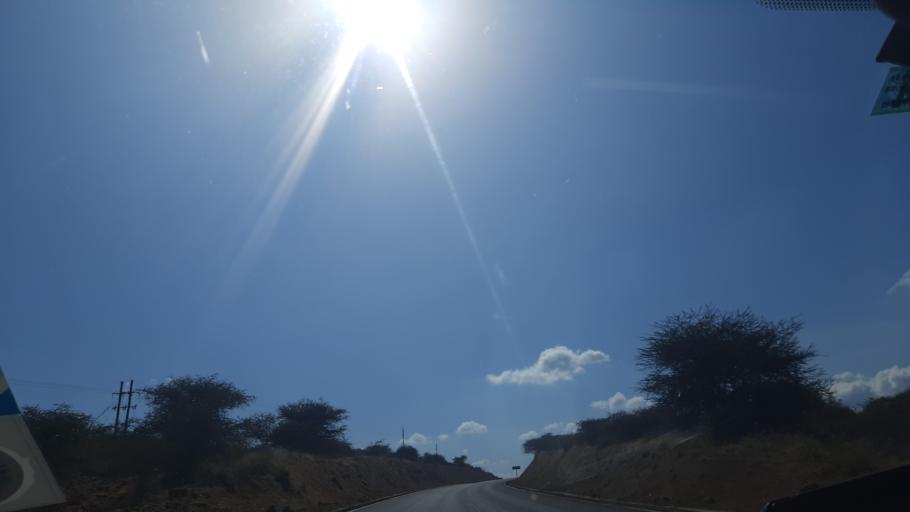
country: TZ
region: Singida
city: Kilimatinde
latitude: -5.7804
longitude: 34.8827
